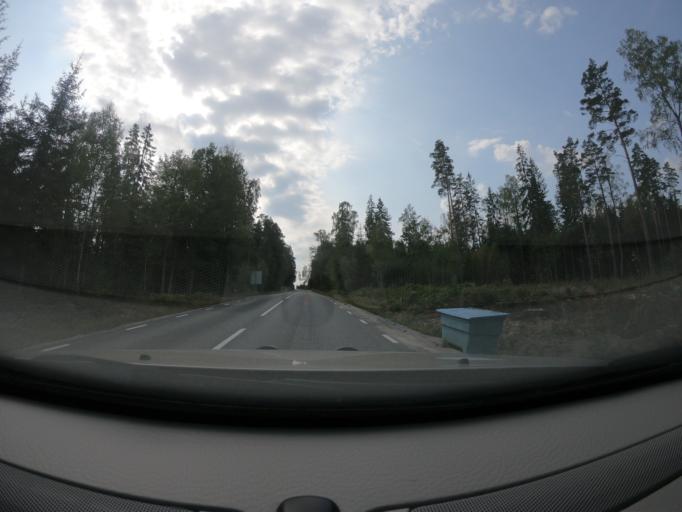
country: SE
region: Kronoberg
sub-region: Vaxjo Kommun
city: Braas
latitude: 57.1814
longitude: 14.9643
